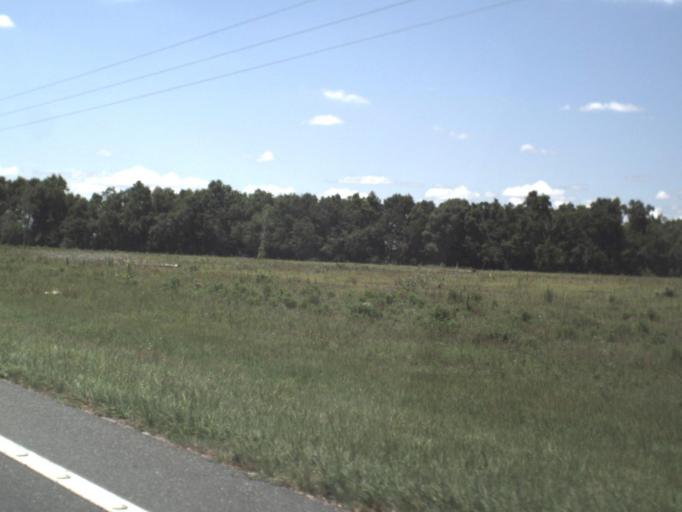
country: US
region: Florida
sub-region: Lafayette County
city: Mayo
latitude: 30.0618
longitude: -83.1904
